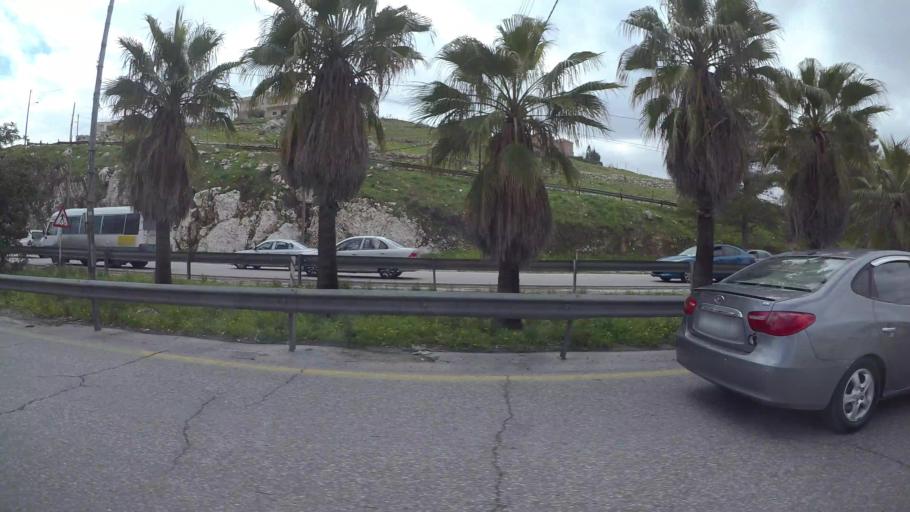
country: JO
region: Balqa
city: As Salt
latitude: 32.0340
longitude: 35.7930
